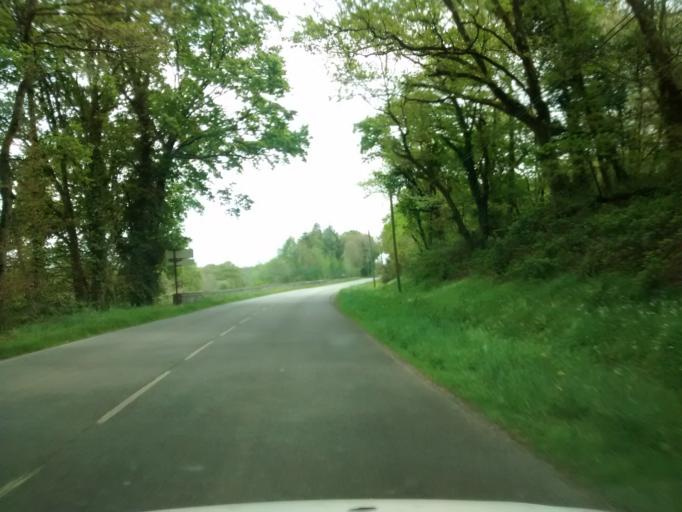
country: FR
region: Brittany
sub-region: Departement du Morbihan
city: Malestroit
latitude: 47.8063
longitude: -2.3691
